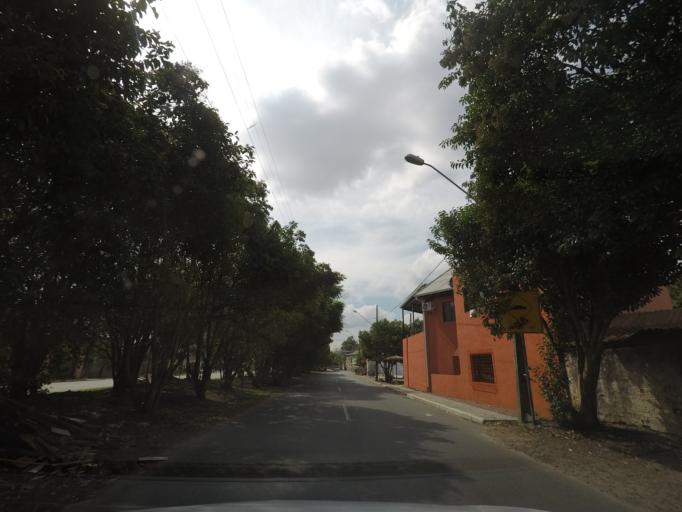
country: BR
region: Parana
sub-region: Pinhais
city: Pinhais
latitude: -25.4648
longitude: -49.1965
